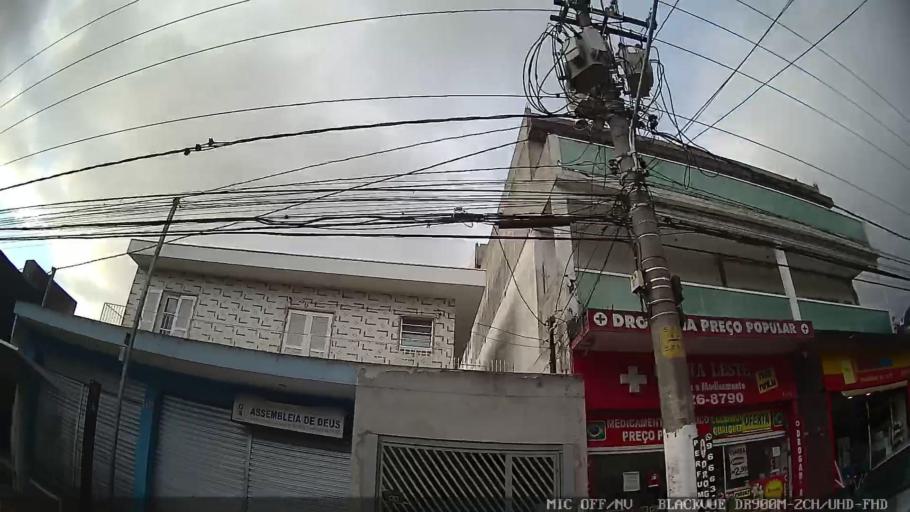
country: BR
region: Sao Paulo
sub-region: Sao Caetano Do Sul
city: Sao Caetano do Sul
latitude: -23.5735
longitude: -46.4937
